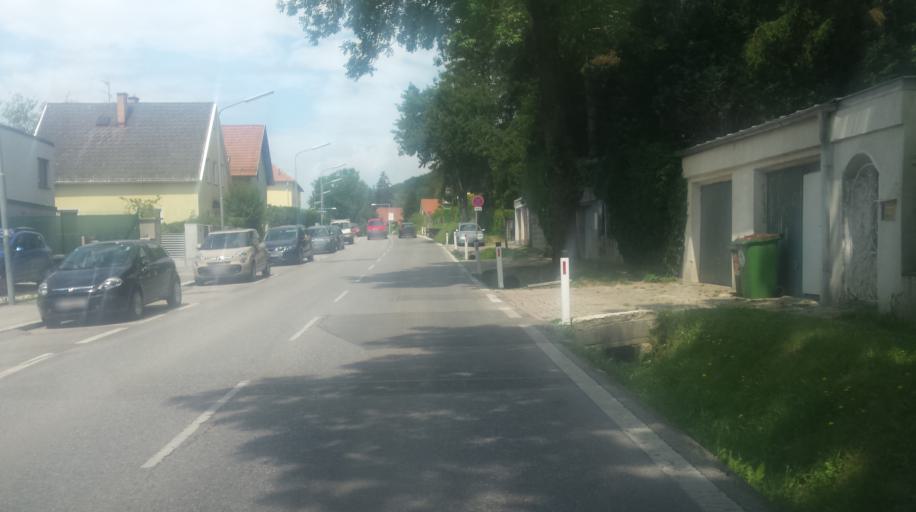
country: AT
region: Lower Austria
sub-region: Politischer Bezirk Wien-Umgebung
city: Purkersdorf
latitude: 48.2271
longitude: 16.2065
